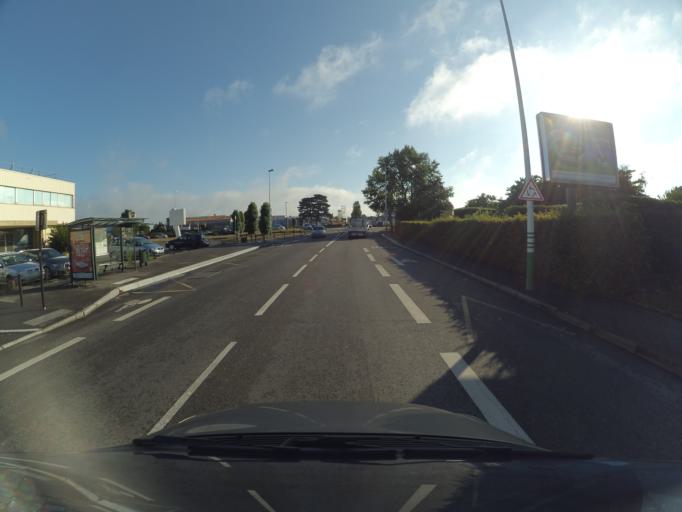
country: FR
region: Pays de la Loire
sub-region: Departement de la Loire-Atlantique
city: Saint-Herblain
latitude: 47.2273
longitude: -1.6363
